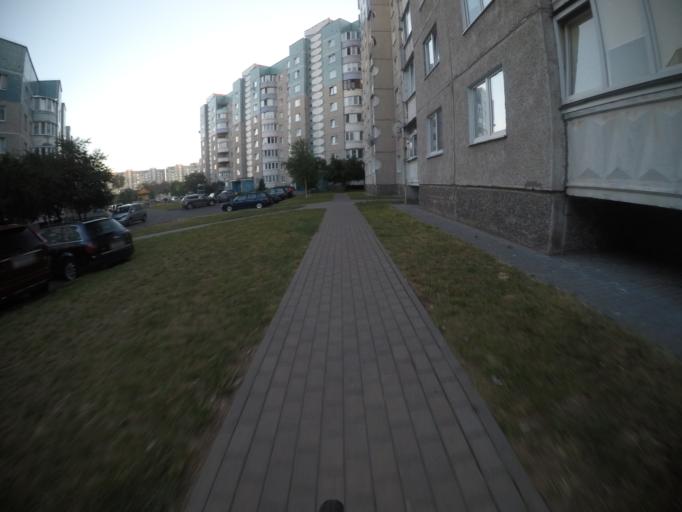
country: BY
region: Grodnenskaya
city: Hrodna
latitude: 53.7038
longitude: 23.8576
